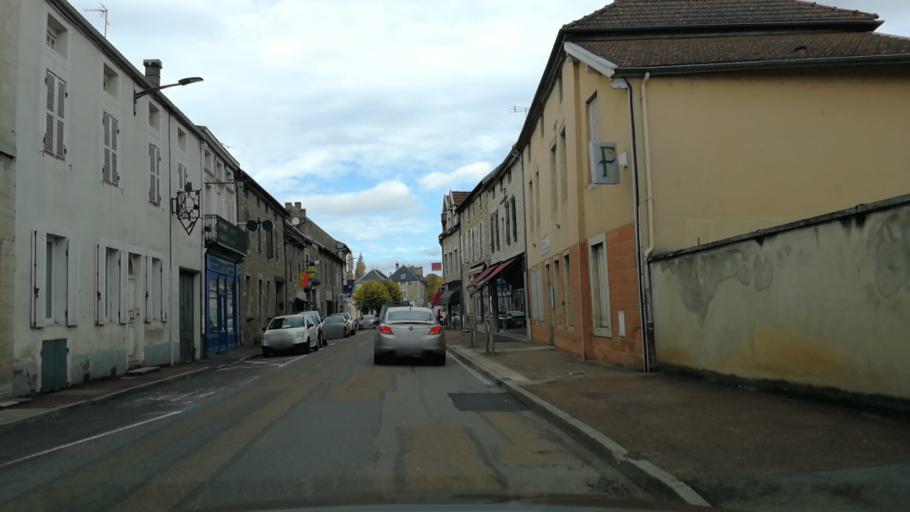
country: FR
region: Bourgogne
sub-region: Departement de la Cote-d'Or
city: Pouilly-en-Auxois
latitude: 47.2615
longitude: 4.5570
